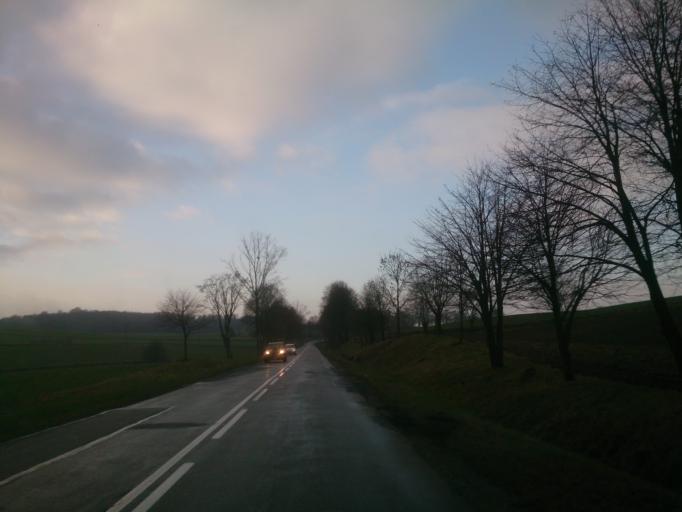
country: PL
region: Pomeranian Voivodeship
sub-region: Powiat bytowski
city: Tuchomie
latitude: 54.1347
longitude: 17.4087
